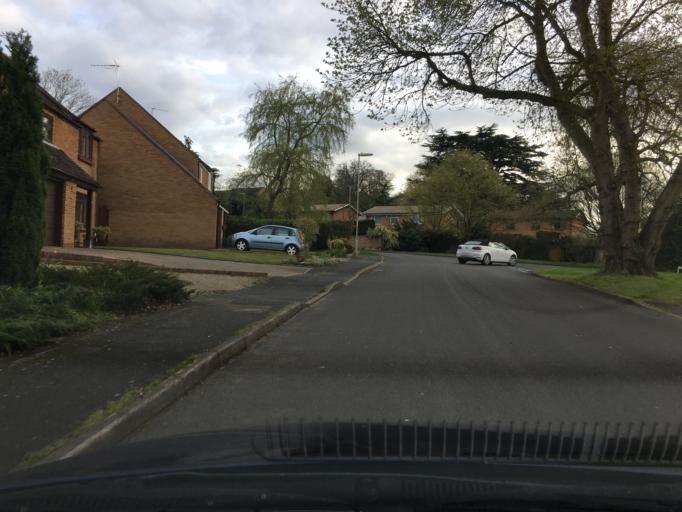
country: GB
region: England
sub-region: Hampshire
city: Yateley
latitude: 51.3368
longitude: -0.8175
